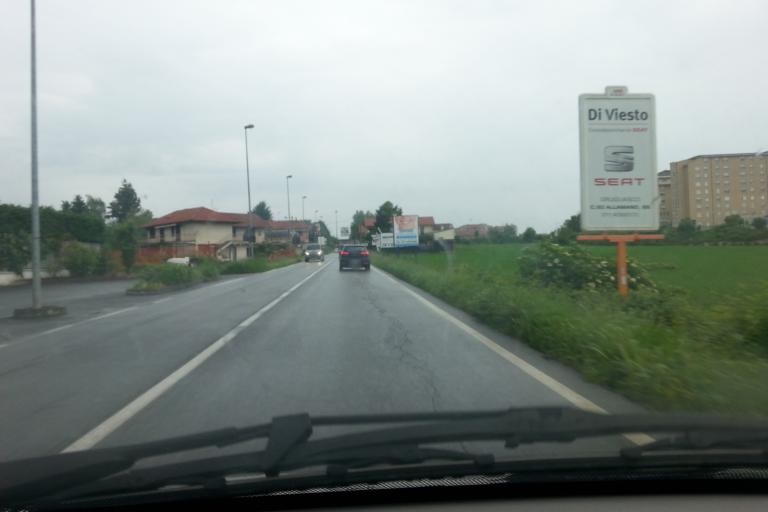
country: IT
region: Piedmont
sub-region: Provincia di Torino
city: Rivoli
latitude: 45.0566
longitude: 7.5196
